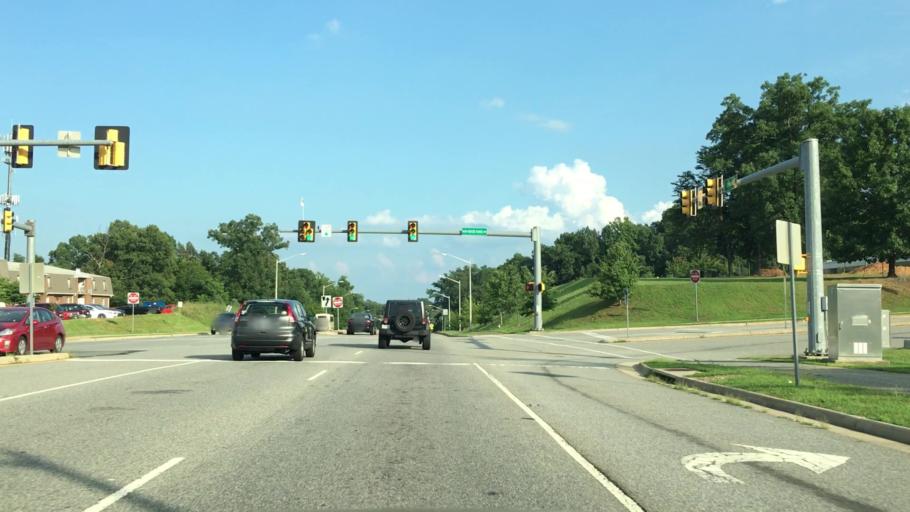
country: US
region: Virginia
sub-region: City of Fredericksburg
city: Fredericksburg
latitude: 38.3043
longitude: -77.4866
